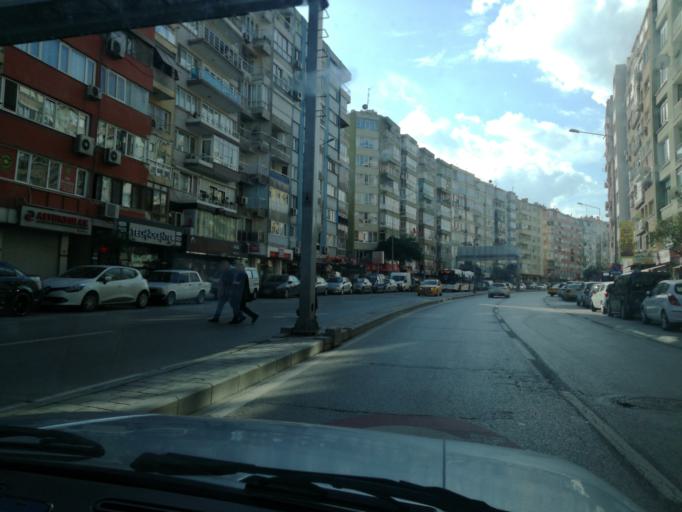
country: TR
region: Izmir
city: Izmir
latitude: 38.4093
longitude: 27.1272
